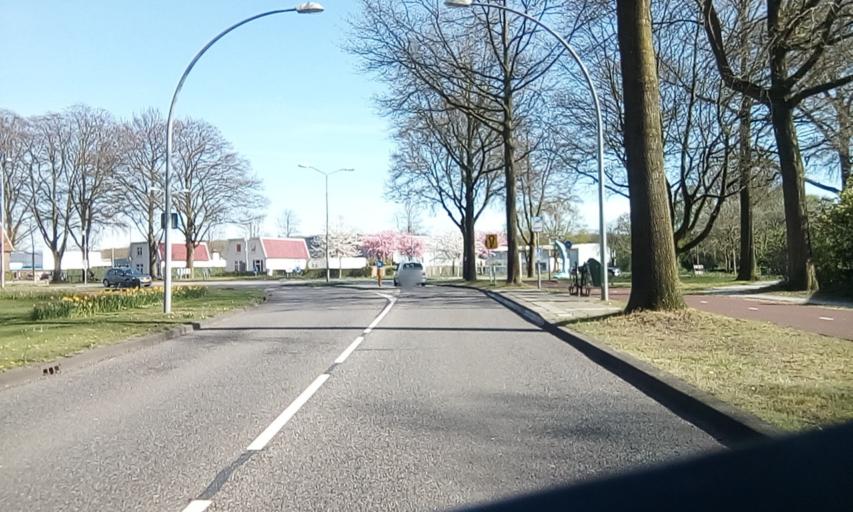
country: NL
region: Gelderland
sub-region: Gemeente Wijchen
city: Wijchen
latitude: 51.8113
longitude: 5.7416
